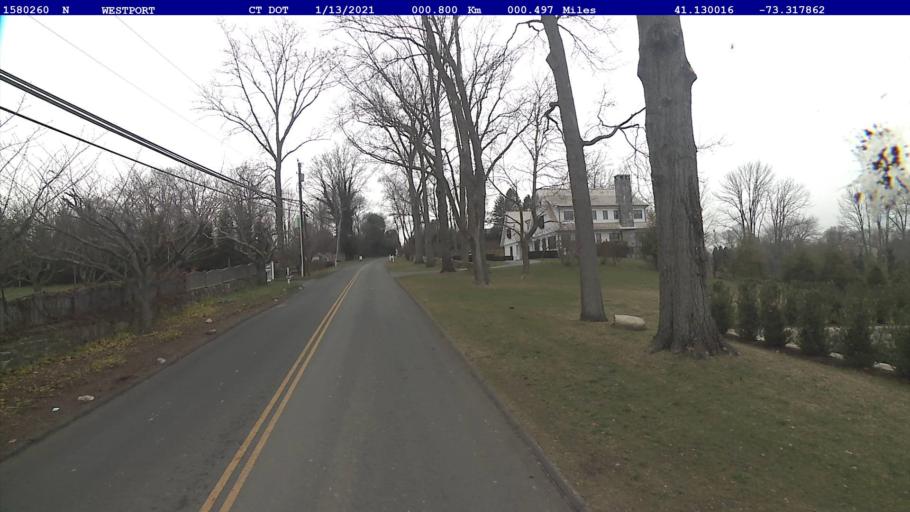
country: US
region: Connecticut
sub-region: Fairfield County
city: Southport
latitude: 41.1300
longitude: -73.3179
